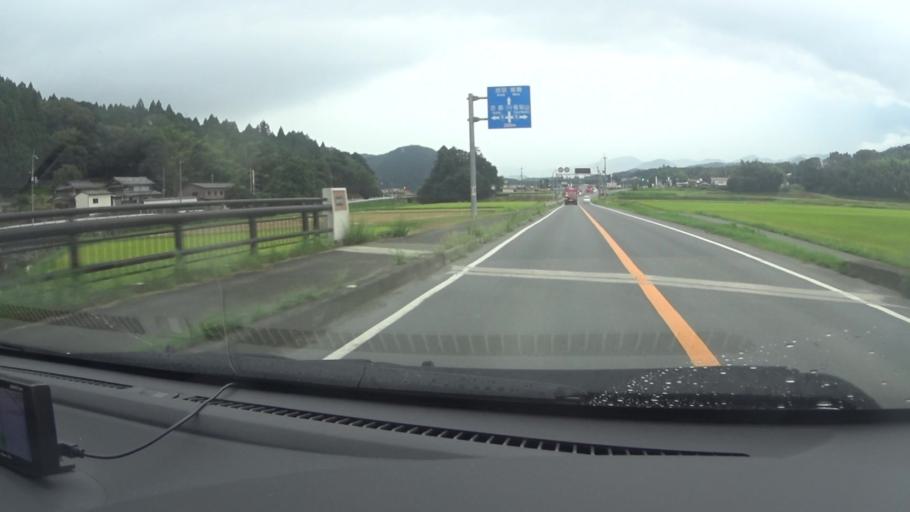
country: JP
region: Kyoto
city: Ayabe
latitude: 35.1851
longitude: 135.3661
